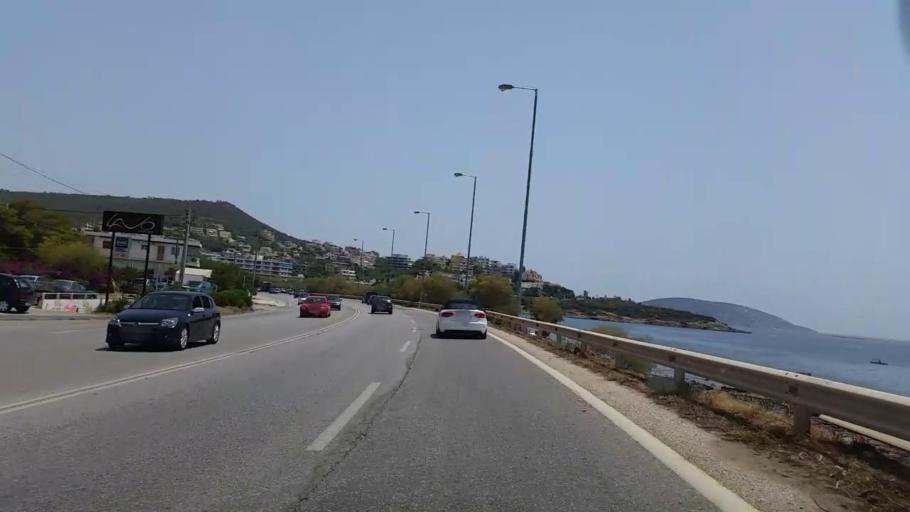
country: GR
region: Attica
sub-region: Nomarchia Anatolikis Attikis
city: Saronida
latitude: 37.7523
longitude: 23.9026
